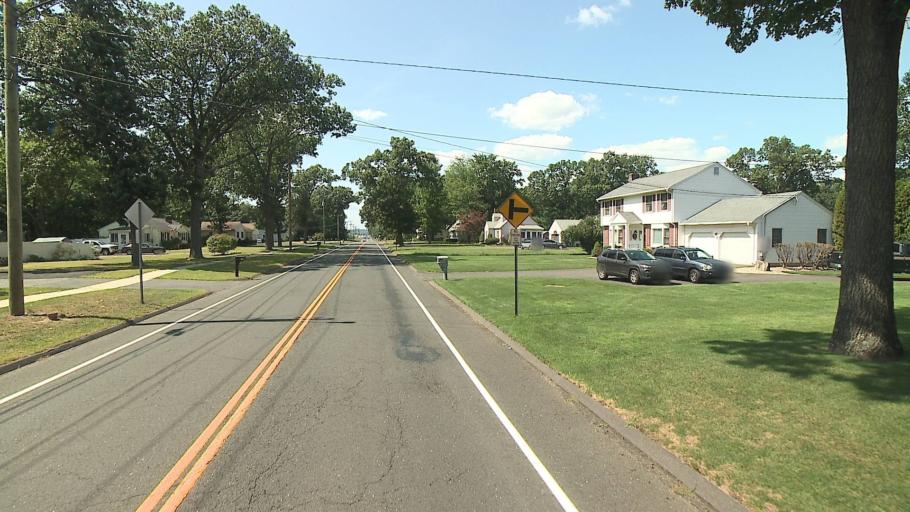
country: US
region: Connecticut
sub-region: Hartford County
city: Windsor Locks
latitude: 41.9274
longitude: -72.6633
